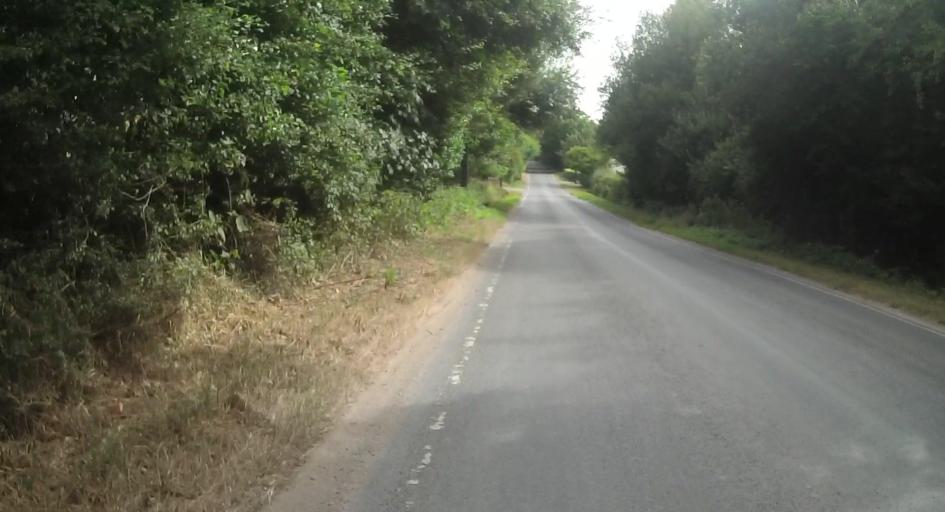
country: GB
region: England
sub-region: Dorset
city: Wareham
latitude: 50.6583
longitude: -2.1165
